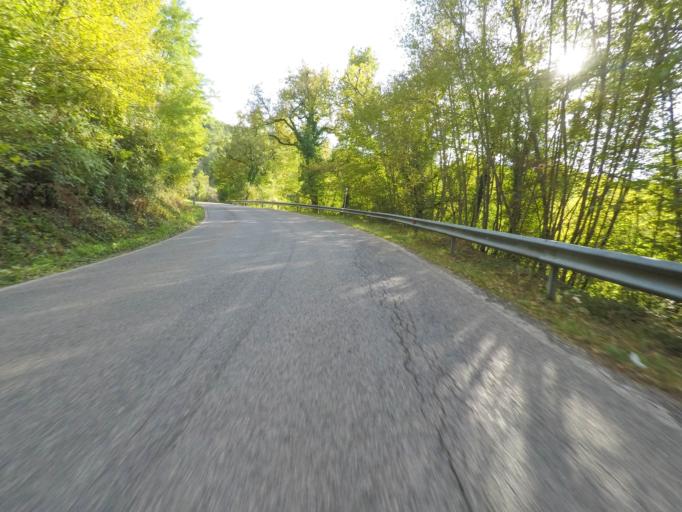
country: IT
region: Tuscany
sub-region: Provincia di Siena
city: Radda in Chianti
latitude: 43.4971
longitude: 11.3923
